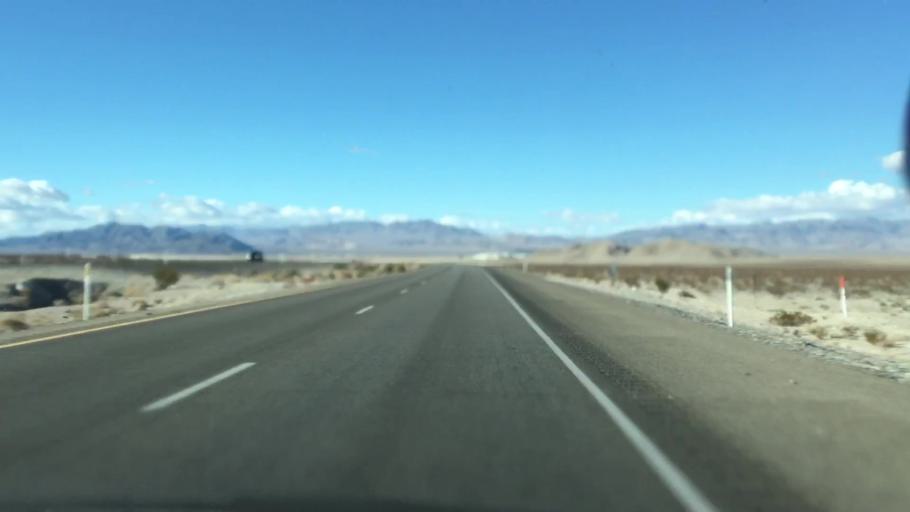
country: US
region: Nevada
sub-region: Nye County
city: Pahrump
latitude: 36.5716
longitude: -115.6302
